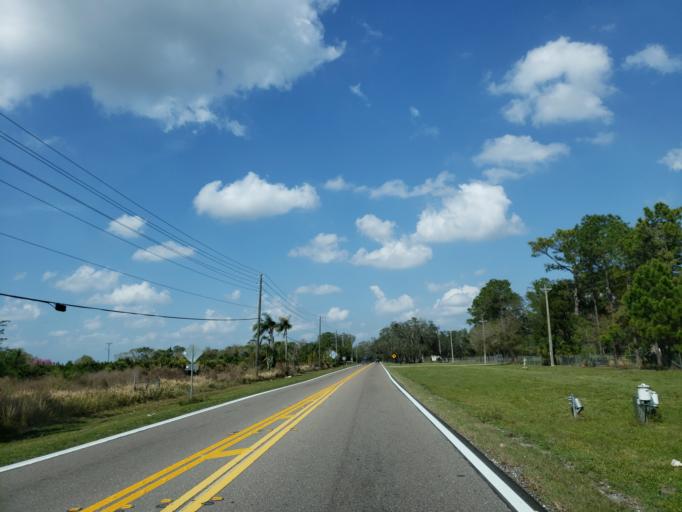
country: US
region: Florida
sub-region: Hillsborough County
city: Keystone
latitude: 28.1368
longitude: -82.5752
